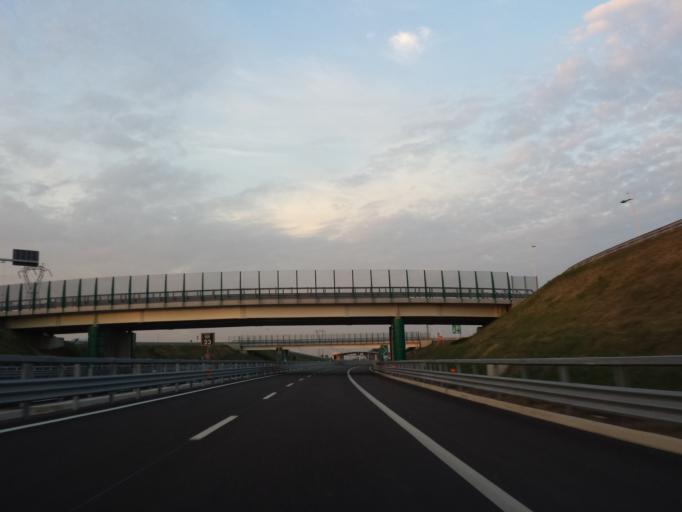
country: IT
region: Veneto
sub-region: Provincia di Vicenza
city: Ponte di Barbarano
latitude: 45.3858
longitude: 11.6132
